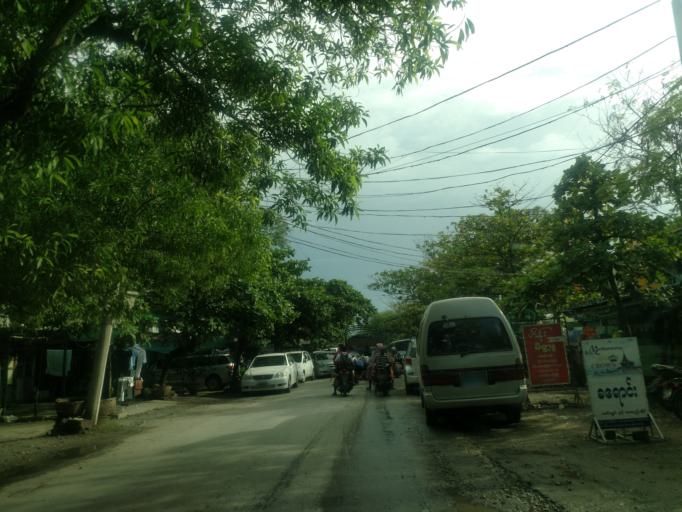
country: MM
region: Mandalay
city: Mandalay
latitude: 21.9772
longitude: 96.1005
